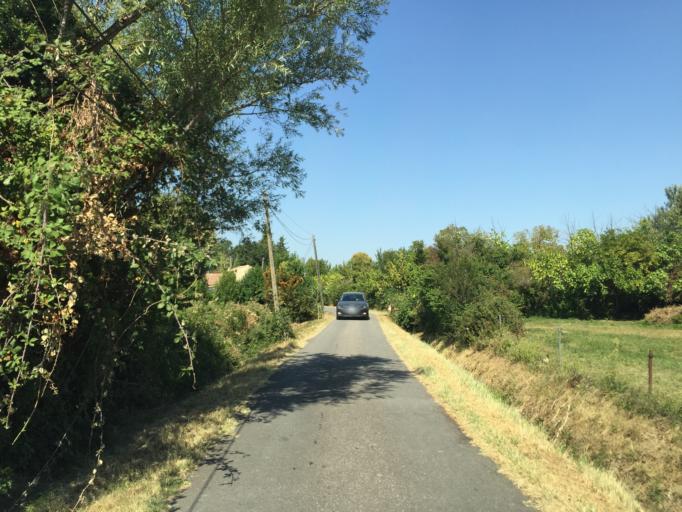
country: FR
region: Provence-Alpes-Cote d'Azur
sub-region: Departement du Vaucluse
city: Orange
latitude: 44.1014
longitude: 4.8165
